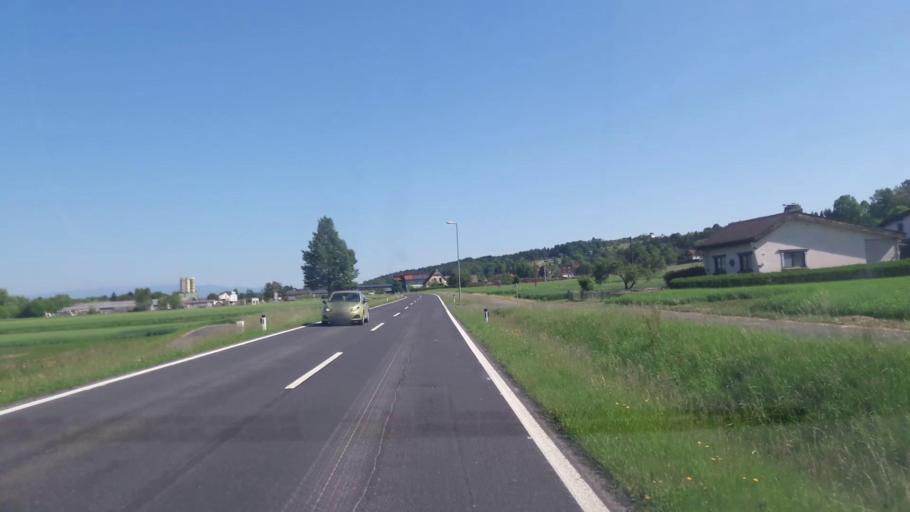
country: AT
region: Styria
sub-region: Politischer Bezirk Hartberg-Fuerstenfeld
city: Burgau
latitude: 47.1456
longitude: 16.1176
